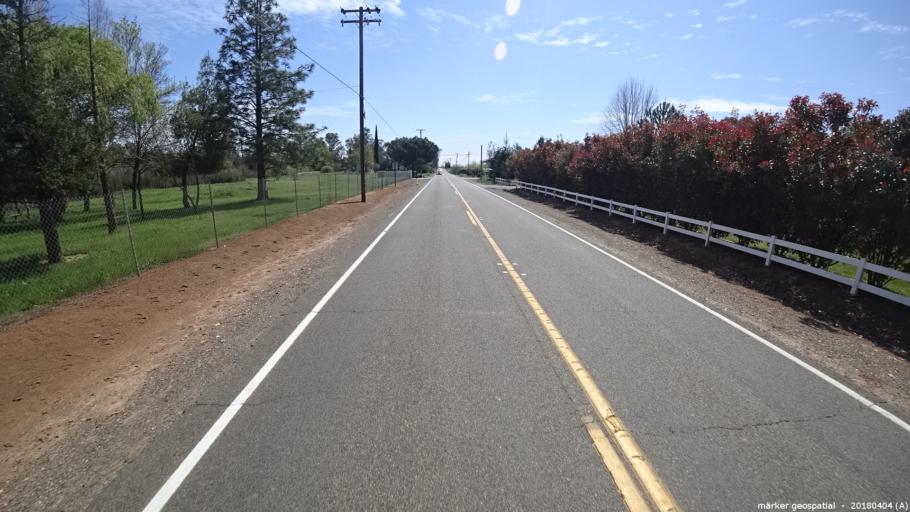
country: US
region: California
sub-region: Sacramento County
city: Herald
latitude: 38.3439
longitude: -121.2238
